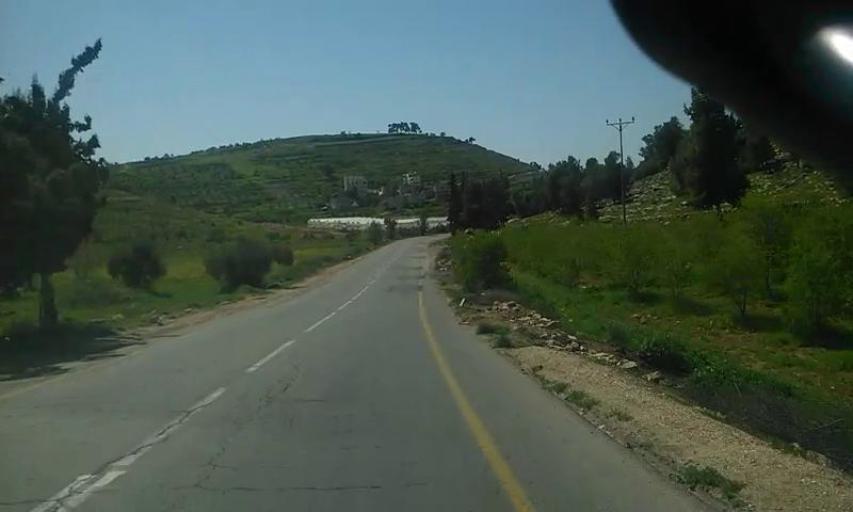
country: PS
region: West Bank
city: Ar Rihiyah
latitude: 31.4883
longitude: 35.0636
